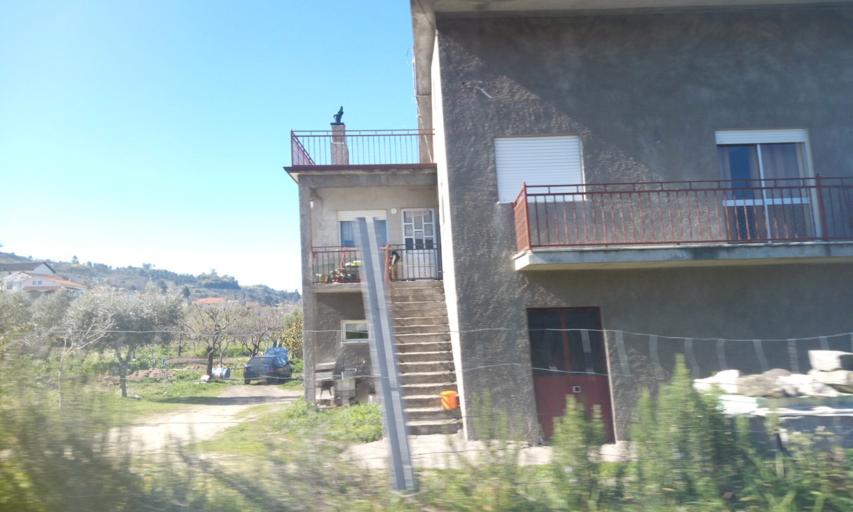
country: PT
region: Guarda
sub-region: Fornos de Algodres
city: Fornos de Algodres
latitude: 40.5225
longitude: -7.5522
